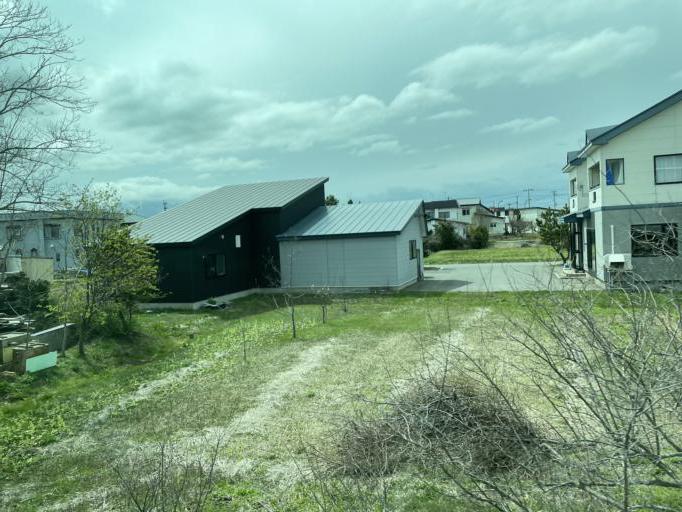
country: JP
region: Aomori
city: Goshogawara
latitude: 40.7631
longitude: 140.4353
